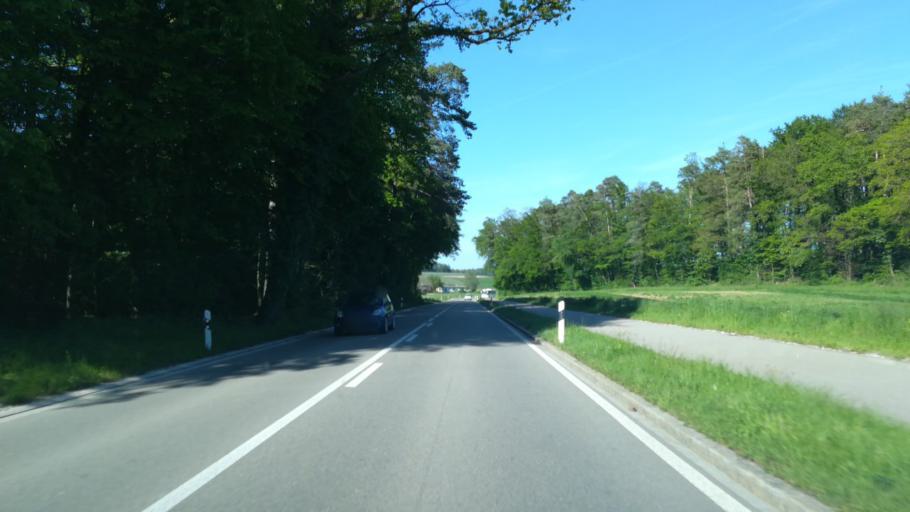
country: CH
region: Zurich
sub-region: Bezirk Andelfingen
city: Kleinandelfingen
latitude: 47.6068
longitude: 8.7046
